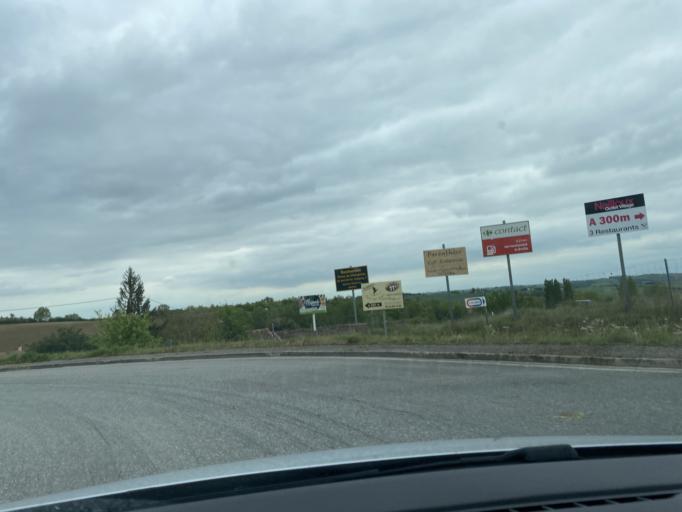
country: FR
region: Midi-Pyrenees
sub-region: Departement de la Haute-Garonne
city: Nailloux
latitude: 43.3808
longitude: 1.6145
